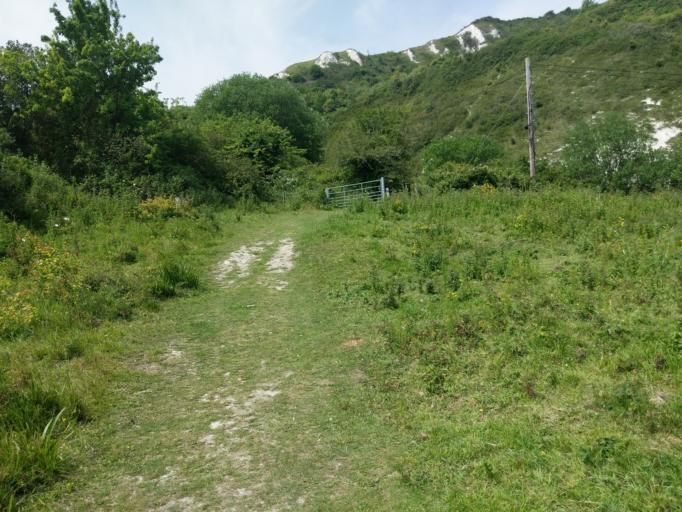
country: GB
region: England
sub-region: Kent
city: Folkestone
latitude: 51.0925
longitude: 1.2026
